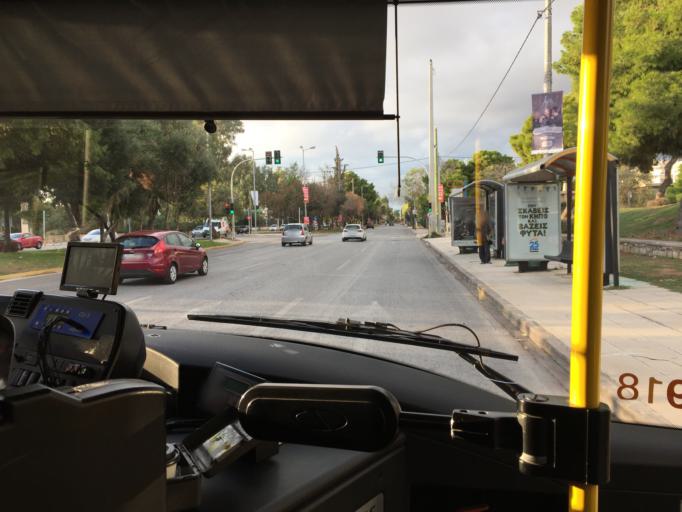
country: GR
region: Attica
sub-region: Nomarchia Athinas
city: Elliniko
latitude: 37.8727
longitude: 23.7361
